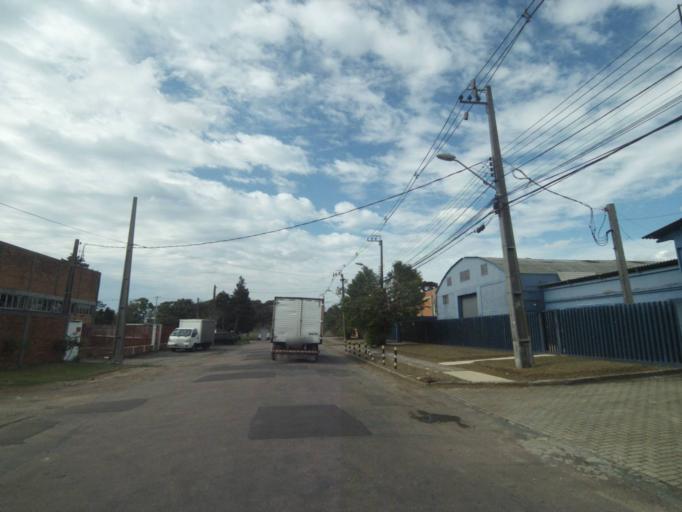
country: BR
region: Parana
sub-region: Curitiba
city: Curitiba
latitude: -25.4971
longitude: -49.3303
